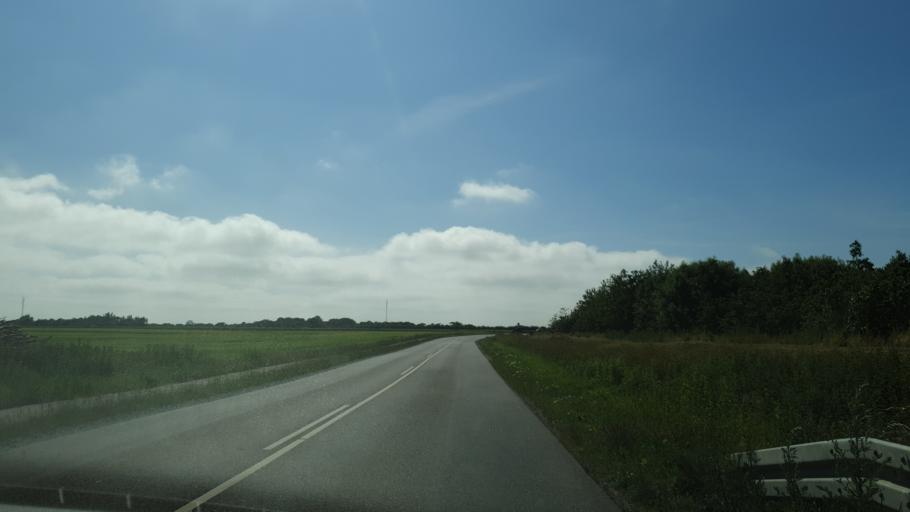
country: DK
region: Central Jutland
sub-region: Ringkobing-Skjern Kommune
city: Ringkobing
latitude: 56.0261
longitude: 8.3616
